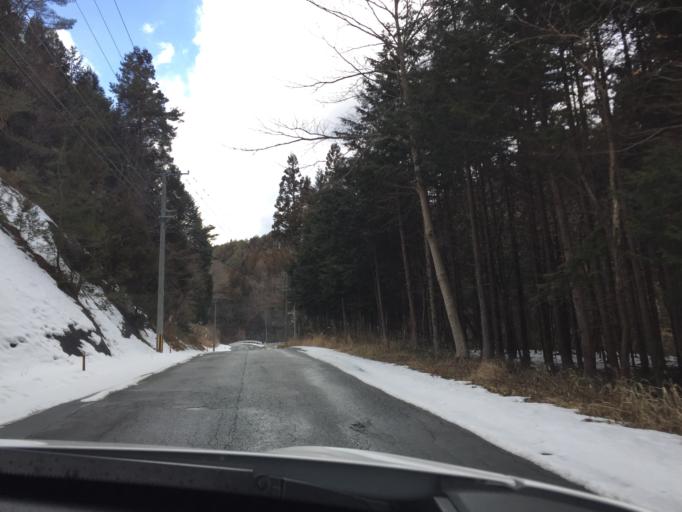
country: JP
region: Fukushima
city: Iwaki
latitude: 37.2236
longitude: 140.7437
